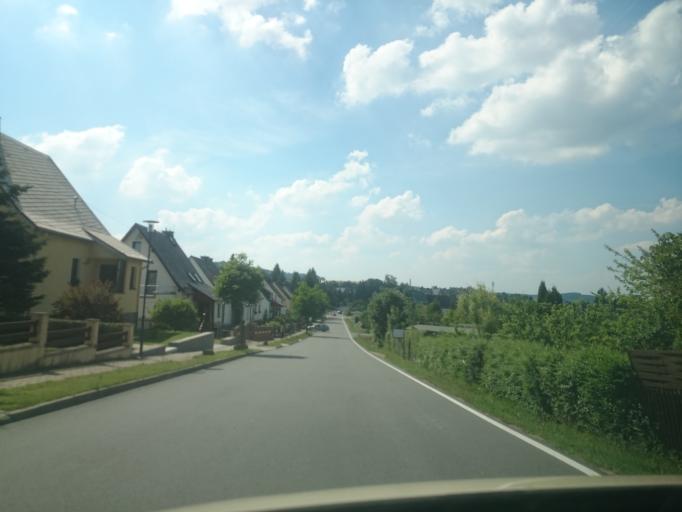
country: DE
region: Saxony
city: Lengefeld
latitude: 50.7148
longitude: 13.2008
